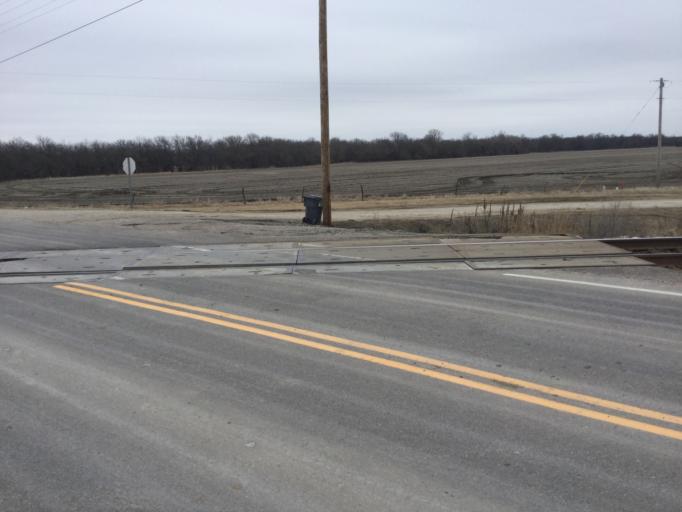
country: US
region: Kansas
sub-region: Butler County
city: Rose Hill
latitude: 37.5485
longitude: -97.1526
